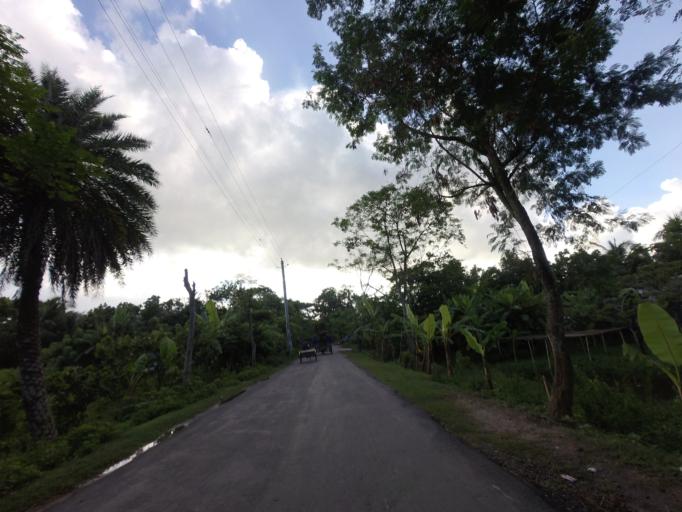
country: BD
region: Khulna
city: Kalia
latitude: 23.0368
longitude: 89.6267
